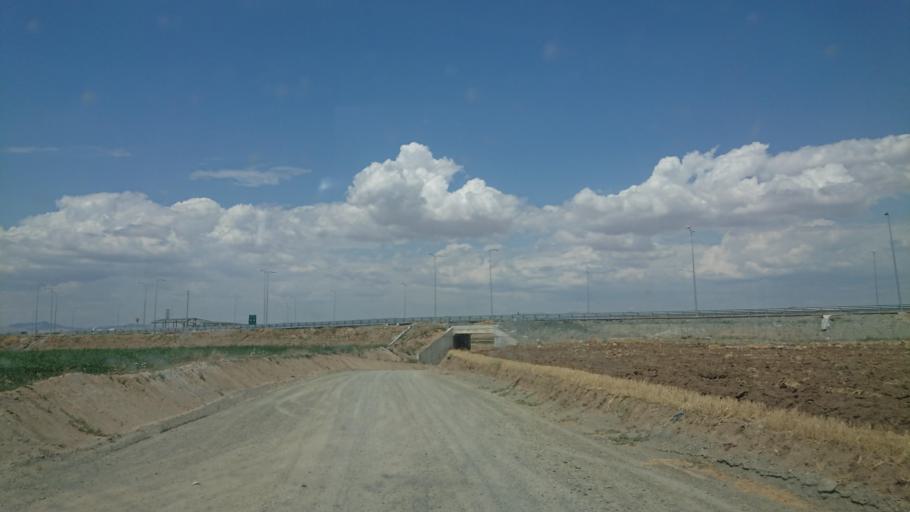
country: TR
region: Aksaray
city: Sariyahsi
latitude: 38.9732
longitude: 33.8989
